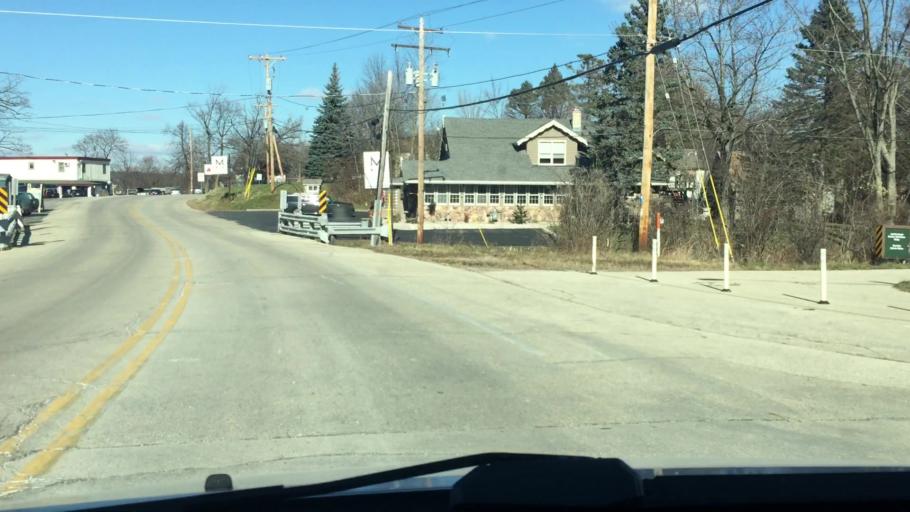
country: US
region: Wisconsin
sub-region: Waukesha County
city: Pewaukee
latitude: 43.0606
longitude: -88.3029
